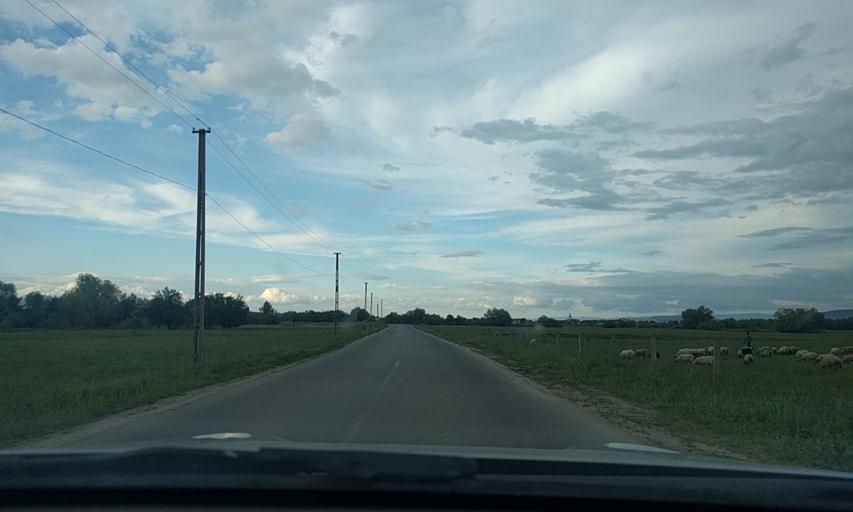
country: RO
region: Brasov
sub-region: Comuna Harman
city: Harman
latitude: 45.7508
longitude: 25.7097
